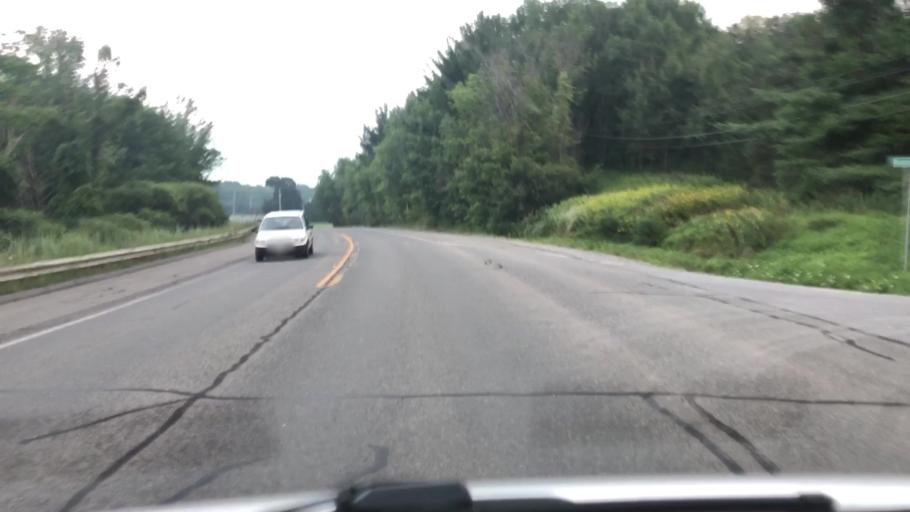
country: US
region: Massachusetts
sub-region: Berkshire County
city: Williamstown
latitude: 42.6400
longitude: -73.2287
